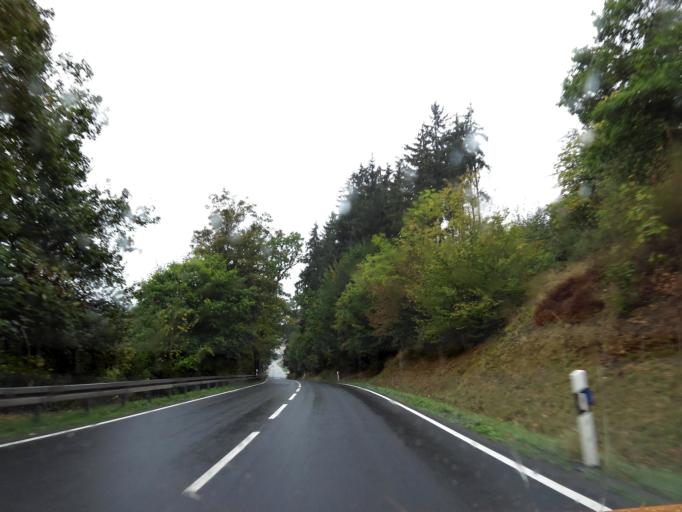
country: DE
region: Saxony-Anhalt
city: Friedrichsbrunn
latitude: 51.6459
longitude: 10.9903
